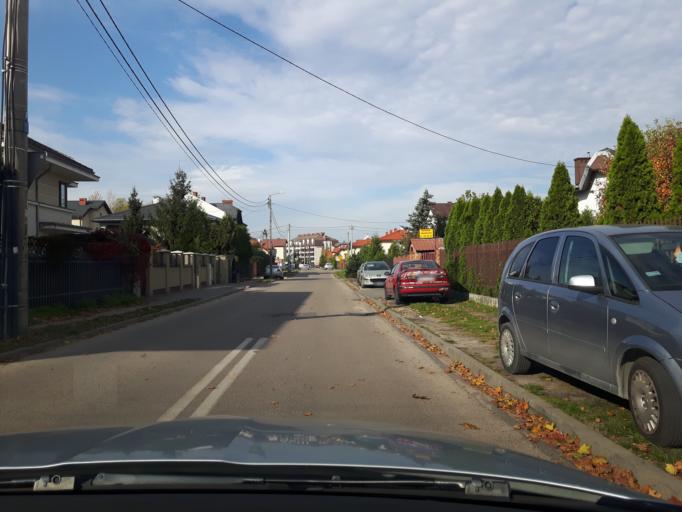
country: PL
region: Masovian Voivodeship
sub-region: Powiat wolominski
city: Zabki
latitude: 52.3035
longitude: 21.1025
